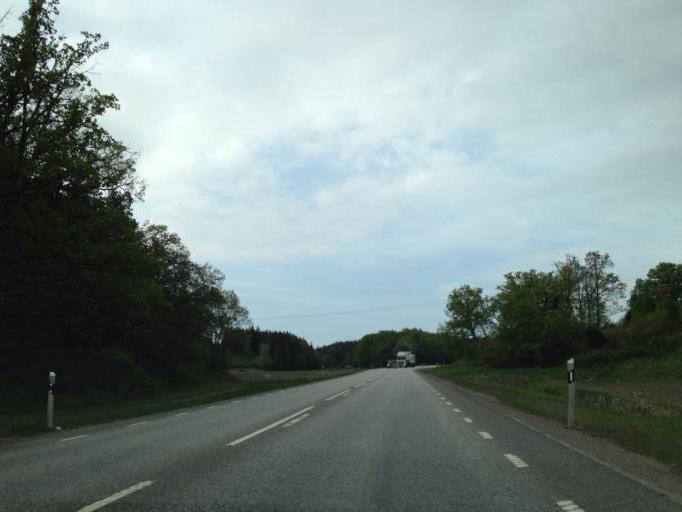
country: SE
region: Soedermanland
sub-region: Eskilstuna Kommun
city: Skogstorp
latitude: 59.3453
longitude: 16.4652
